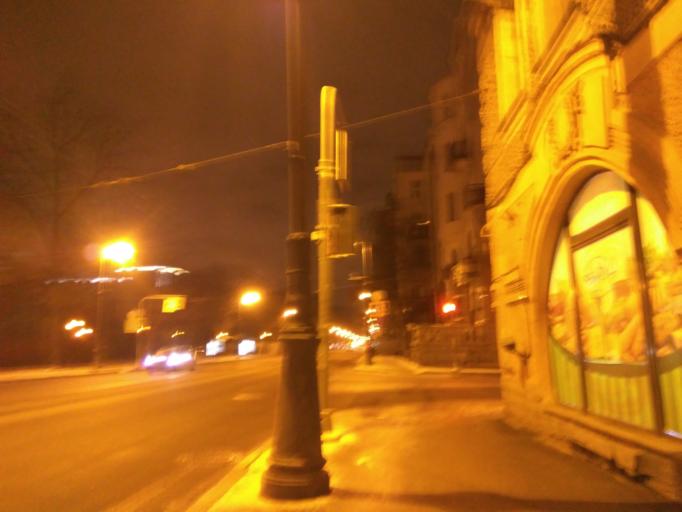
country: RU
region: St.-Petersburg
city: Petrogradka
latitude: 59.9724
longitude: 30.3055
